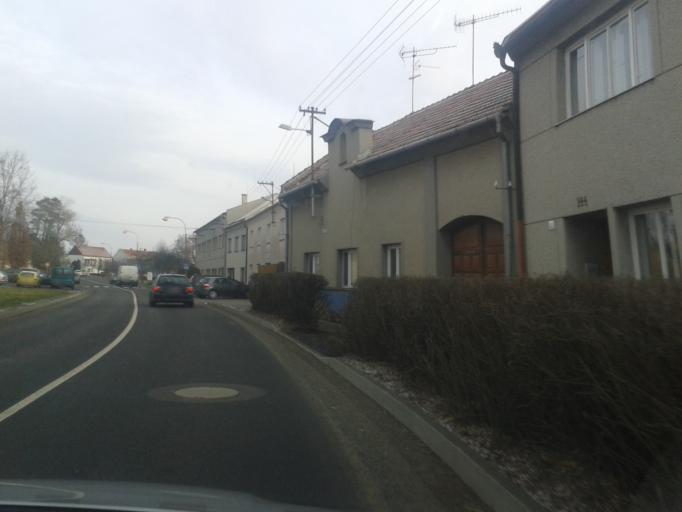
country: CZ
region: Olomoucky
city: Smrzice
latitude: 49.5049
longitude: 17.1020
